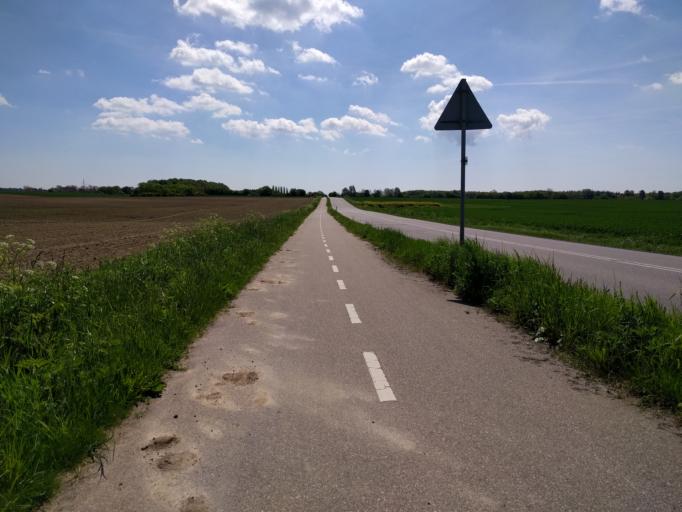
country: DK
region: Zealand
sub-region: Guldborgsund Kommune
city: Nykobing Falster
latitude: 54.7567
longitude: 11.9280
